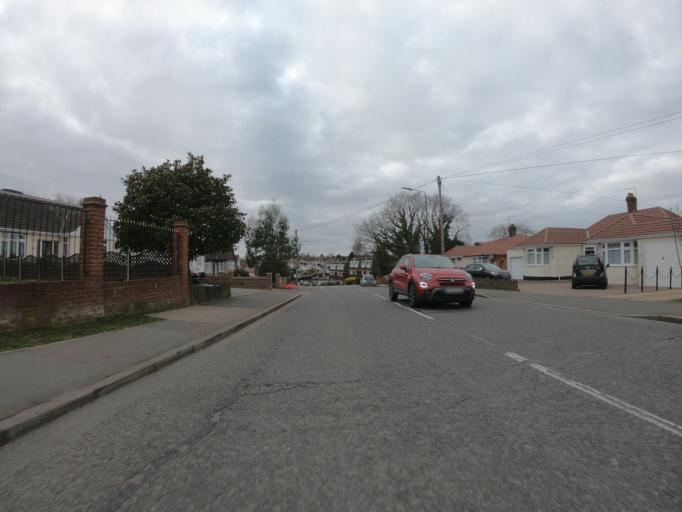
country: GB
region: England
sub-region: Greater London
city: Belvedere
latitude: 51.4788
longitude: 0.1592
